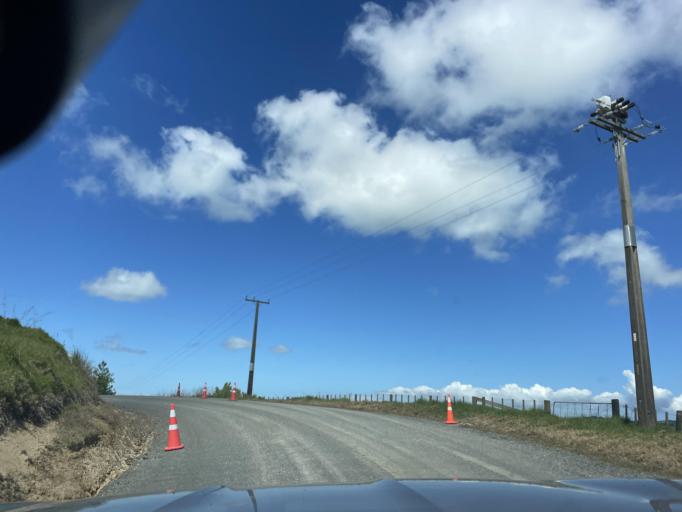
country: NZ
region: Auckland
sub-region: Auckland
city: Wellsford
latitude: -36.2766
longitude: 174.3666
